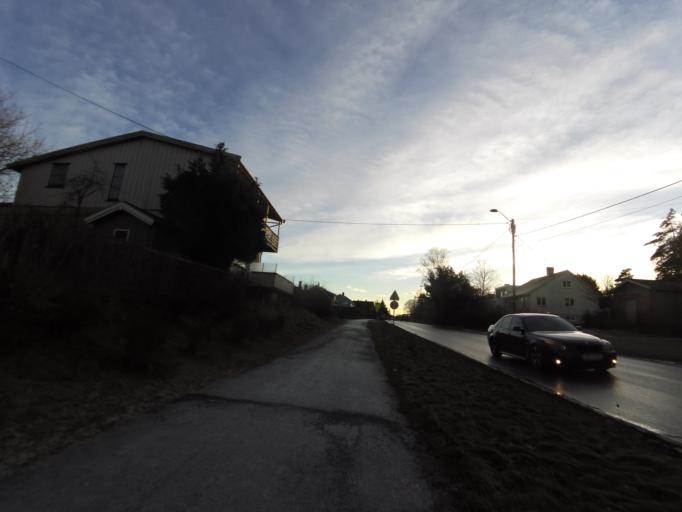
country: NO
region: Ostfold
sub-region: Fredrikstad
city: Fredrikstad
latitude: 59.2256
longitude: 10.9104
